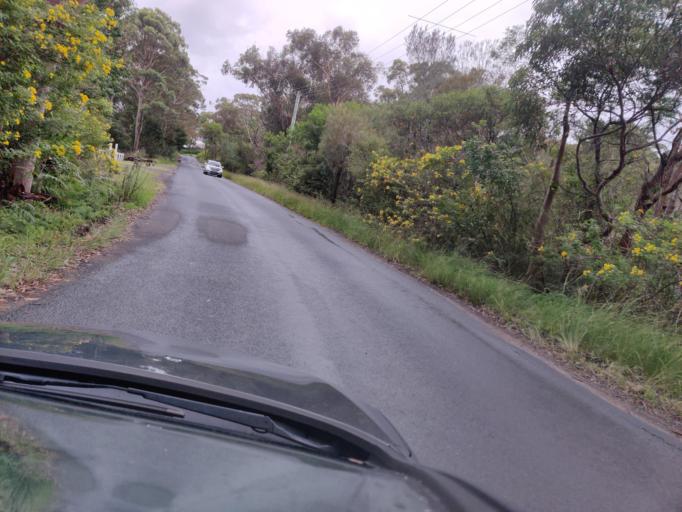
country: AU
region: New South Wales
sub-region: Pittwater
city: Ingleside
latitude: -33.6805
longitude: 151.2537
